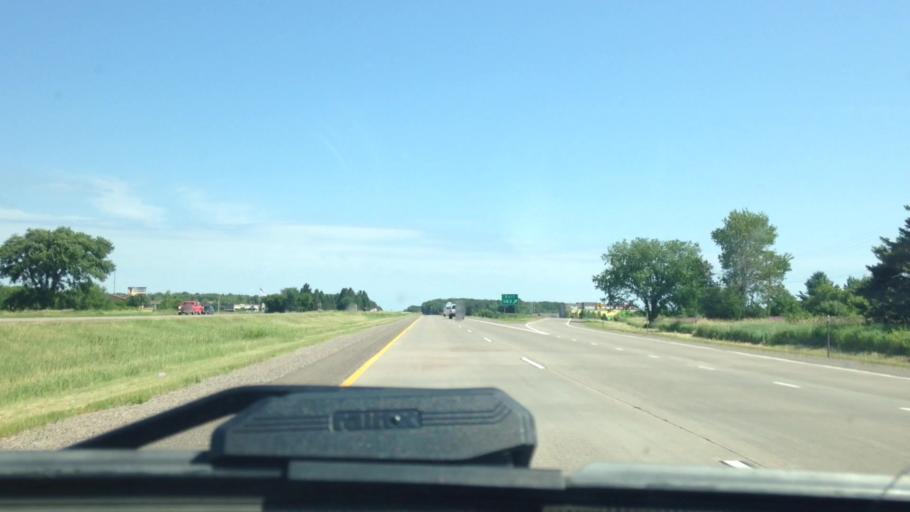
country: US
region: Wisconsin
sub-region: Barron County
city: Rice Lake
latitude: 45.5037
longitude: -91.7631
